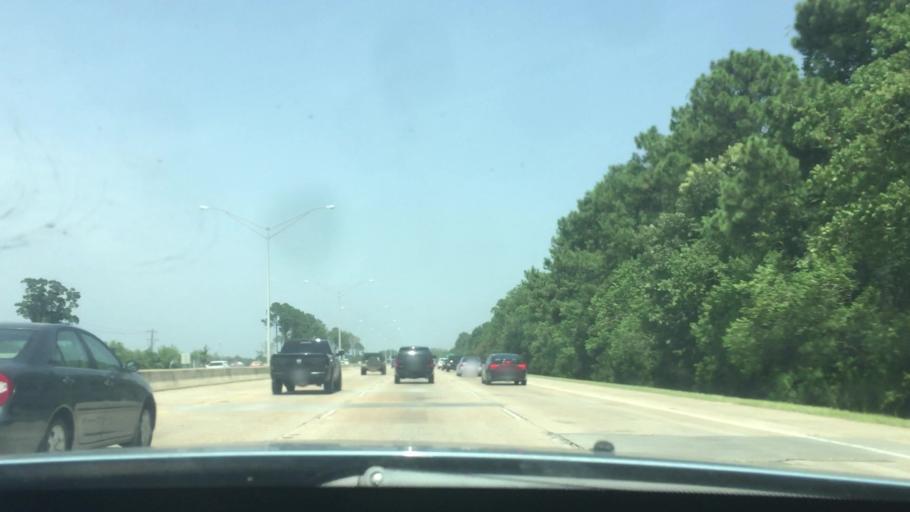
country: US
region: Louisiana
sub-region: East Baton Rouge Parish
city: Shenandoah
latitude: 30.4352
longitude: -91.0359
